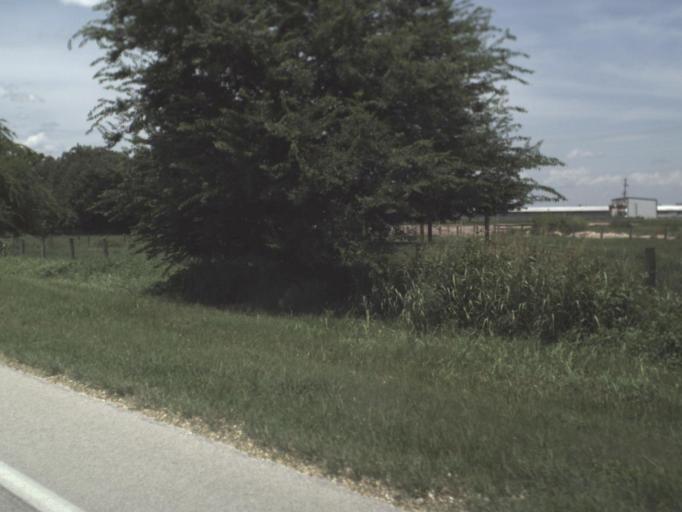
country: US
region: Florida
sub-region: Gilchrist County
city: Trenton
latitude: 29.7259
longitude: -82.8577
